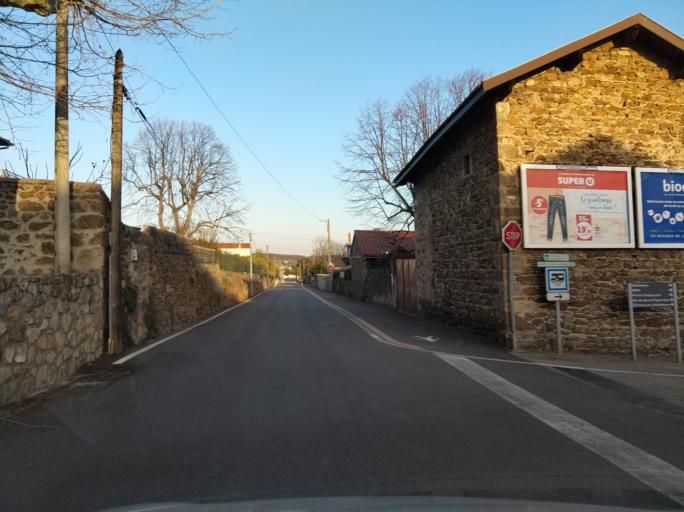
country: FR
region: Rhone-Alpes
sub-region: Departement de l'Ardeche
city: Boulieu-les-Annonay
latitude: 45.2713
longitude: 4.6690
